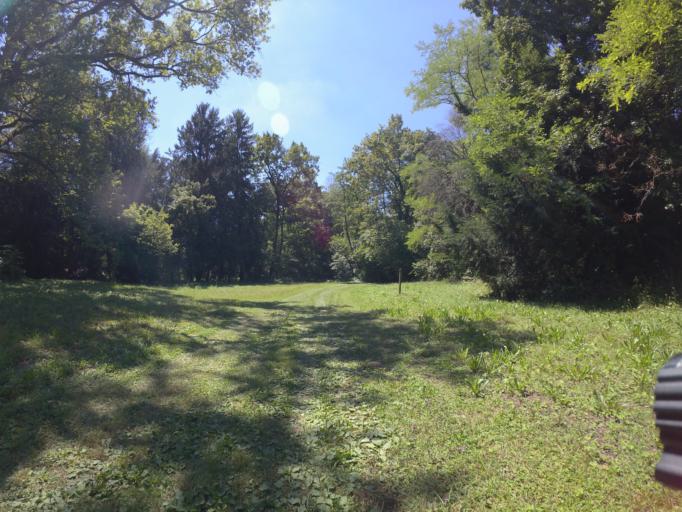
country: IT
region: Friuli Venezia Giulia
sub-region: Provincia di Udine
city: Teor
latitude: 45.8740
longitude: 13.0817
